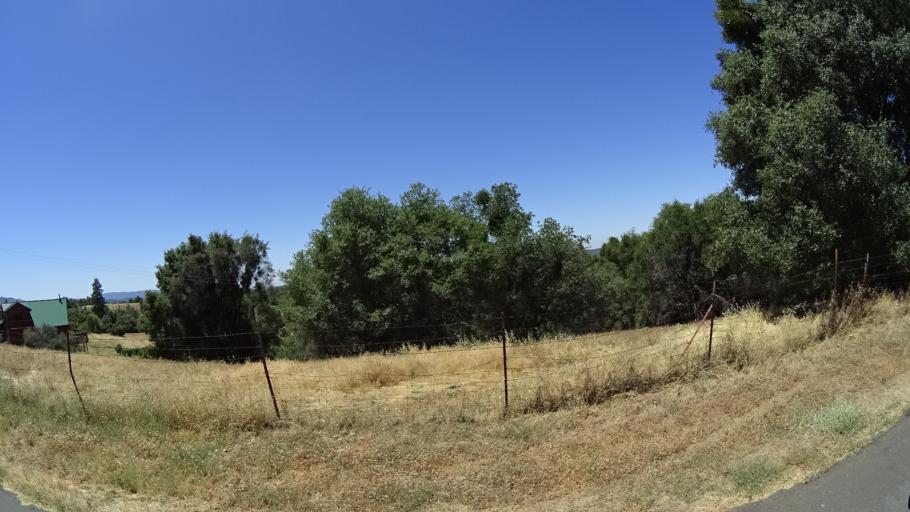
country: US
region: California
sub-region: Amador County
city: Pine Grove
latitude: 38.3405
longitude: -120.6123
